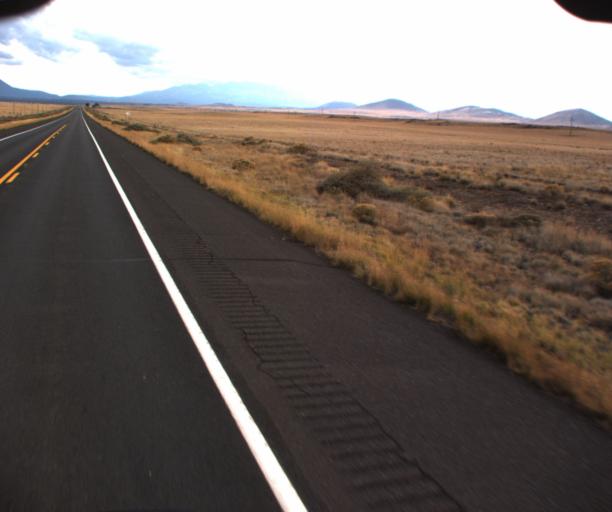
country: US
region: Arizona
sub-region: Coconino County
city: Flagstaff
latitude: 35.6088
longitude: -111.5243
